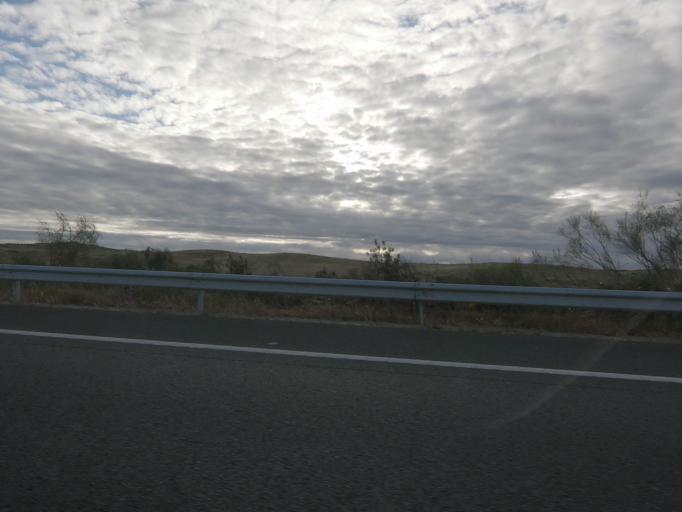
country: ES
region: Extremadura
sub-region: Provincia de Caceres
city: Canaveral
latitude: 39.7635
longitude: -6.3986
